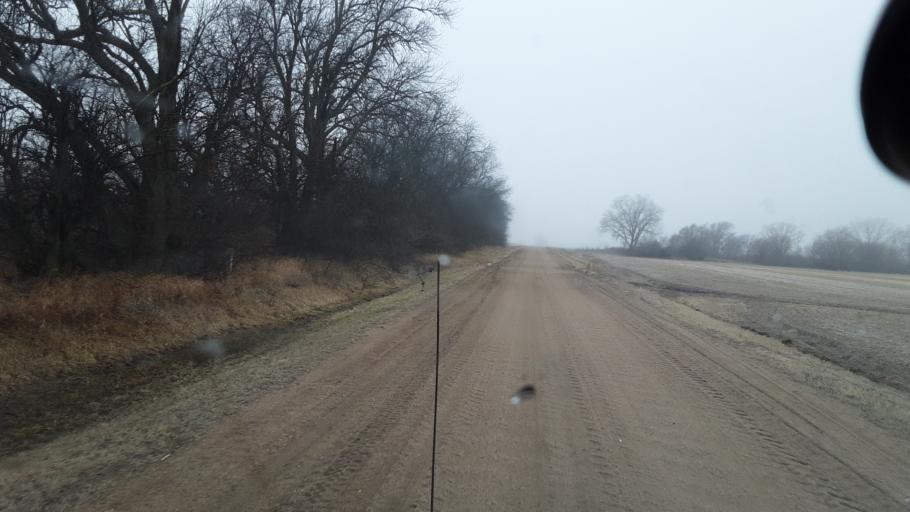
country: US
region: Kansas
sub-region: Reno County
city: South Hutchinson
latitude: 37.9554
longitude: -97.9467
